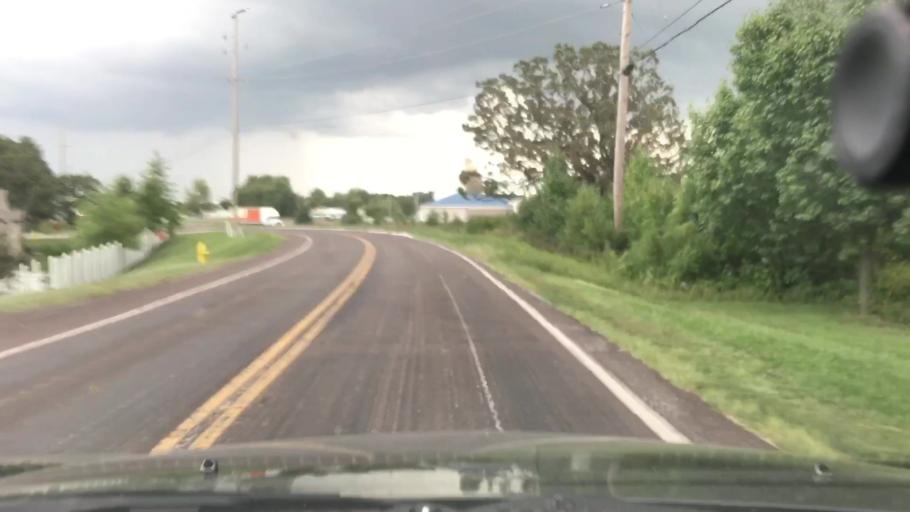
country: US
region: Missouri
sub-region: Saint Charles County
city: Wentzville
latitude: 38.8056
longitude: -90.8898
